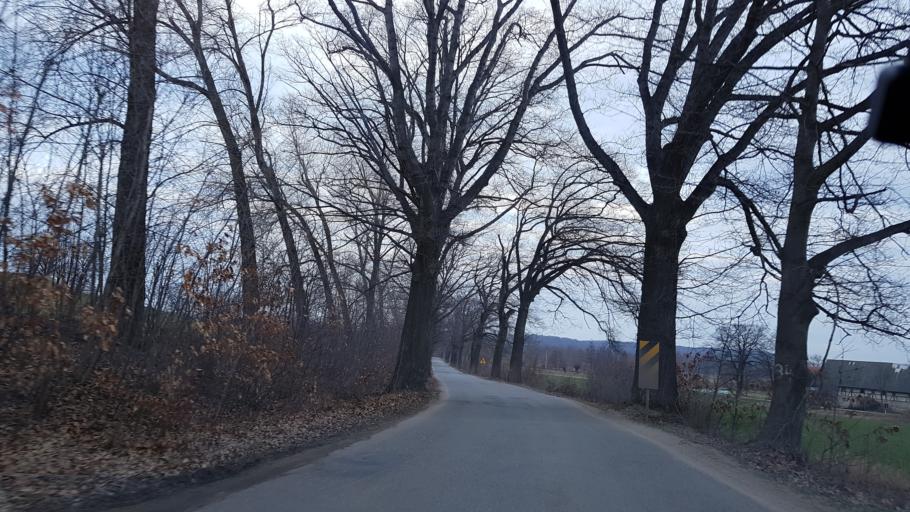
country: PL
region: Lower Silesian Voivodeship
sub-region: Powiat zabkowicki
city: Kamieniec Zabkowicki
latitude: 50.5037
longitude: 16.8611
